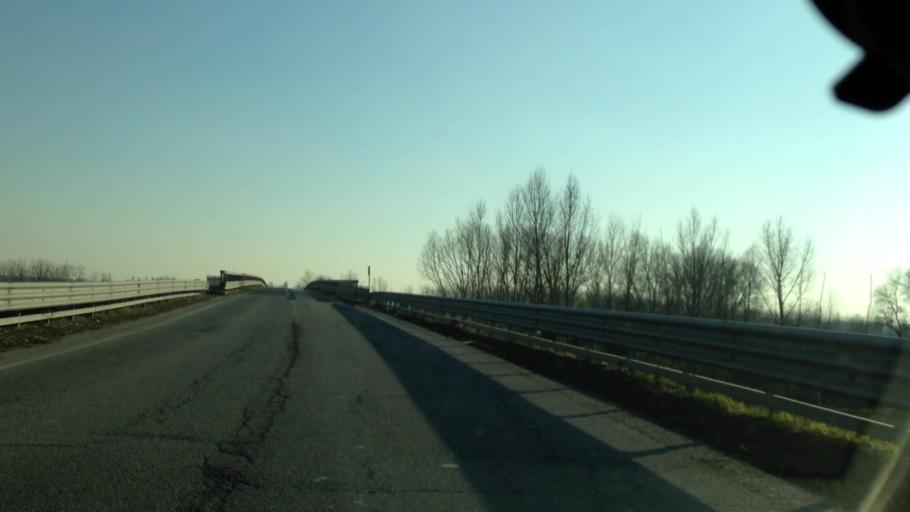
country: IT
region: Piedmont
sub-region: Provincia di Alessandria
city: Felizzano
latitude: 44.8916
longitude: 8.4383
